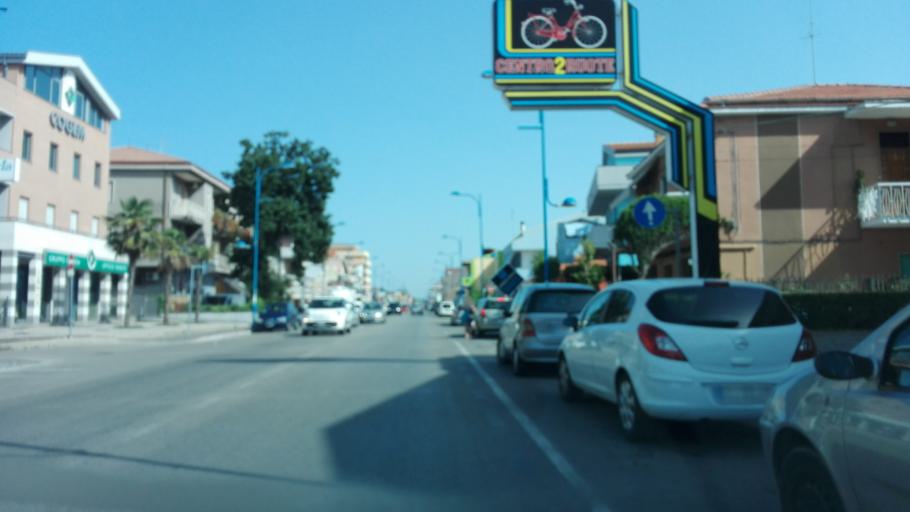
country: IT
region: Abruzzo
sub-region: Provincia di Pescara
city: Montesilvano Marina
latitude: 42.5011
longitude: 14.1686
